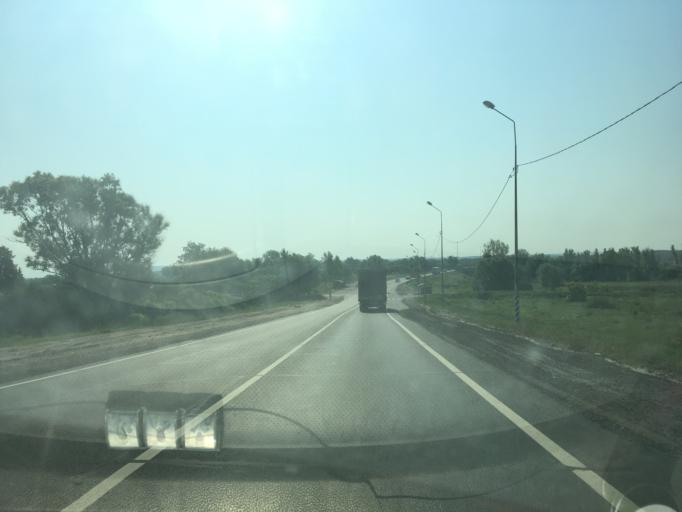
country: RU
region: Nizjnij Novgorod
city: Kstovo
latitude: 56.1005
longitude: 44.3043
